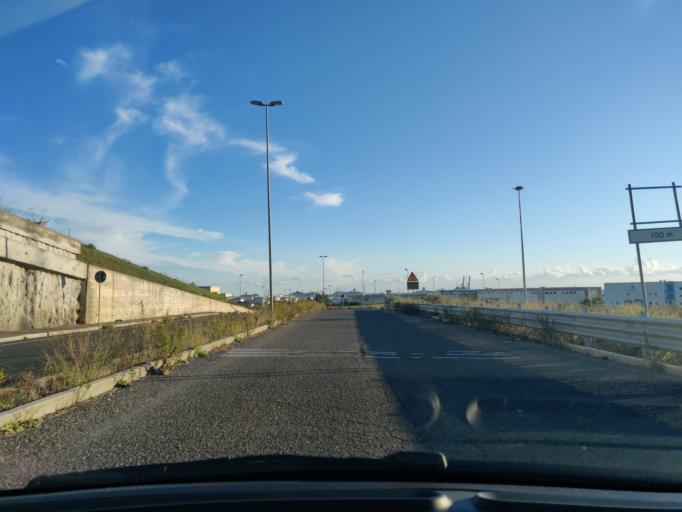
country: IT
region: Latium
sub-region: Citta metropolitana di Roma Capitale
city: Aurelia
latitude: 42.1259
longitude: 11.7780
